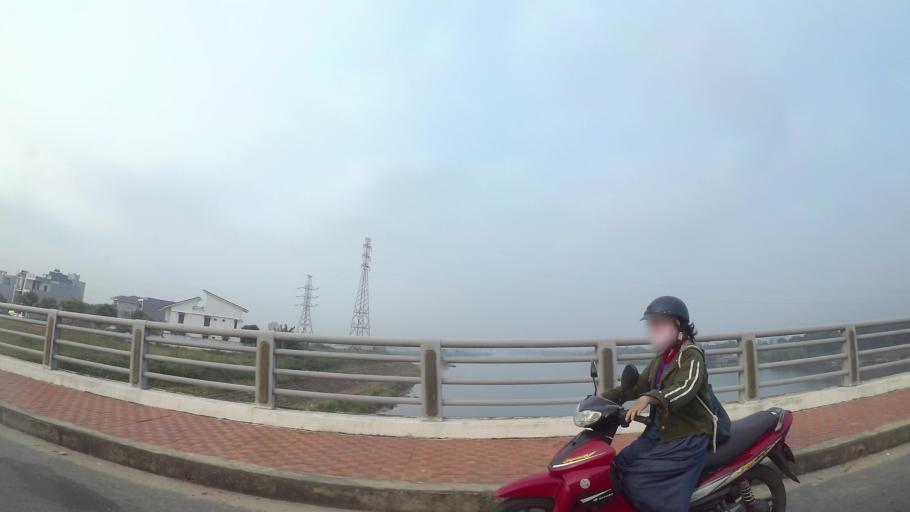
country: VN
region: Da Nang
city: Cam Le
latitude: 16.0236
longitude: 108.2238
